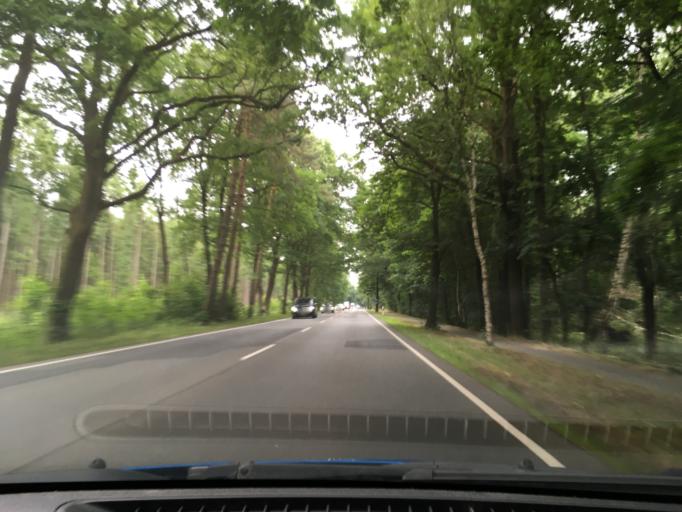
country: DE
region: Lower Saxony
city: Tostedt
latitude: 53.2980
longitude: 9.7420
